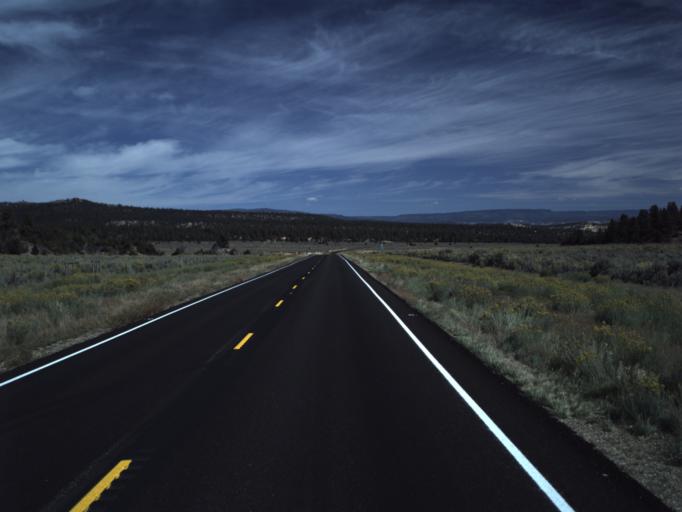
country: US
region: Utah
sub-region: Garfield County
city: Panguitch
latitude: 37.6630
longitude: -111.8327
